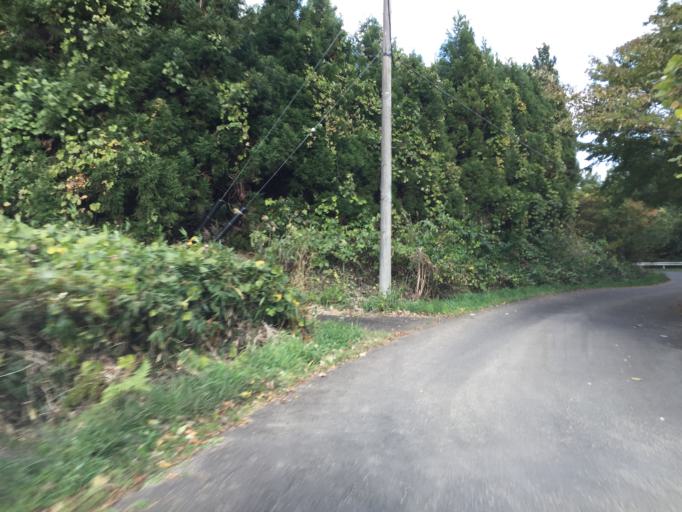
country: JP
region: Fukushima
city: Fukushima-shi
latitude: 37.7082
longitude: 140.3350
